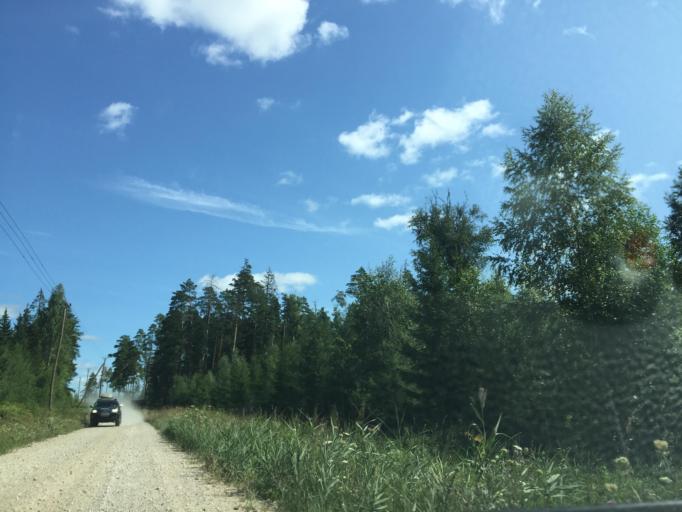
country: LV
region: Talsu Rajons
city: Stende
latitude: 57.1805
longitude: 22.3159
